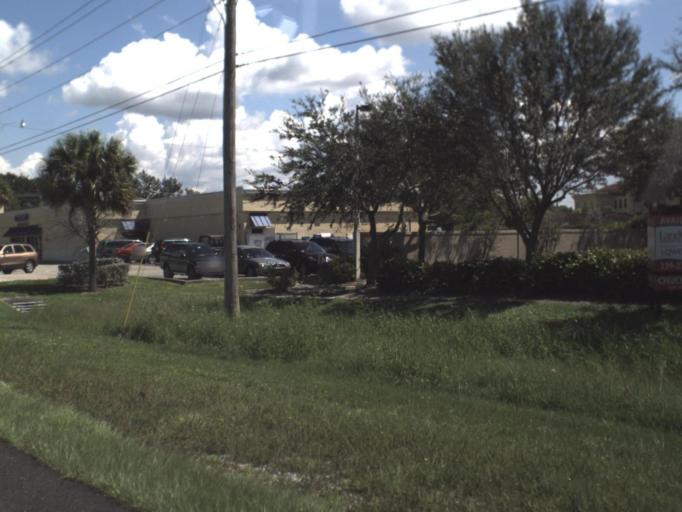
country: US
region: Florida
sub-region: Lee County
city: Lochmoor Waterway Estates
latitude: 26.6659
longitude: -81.9443
